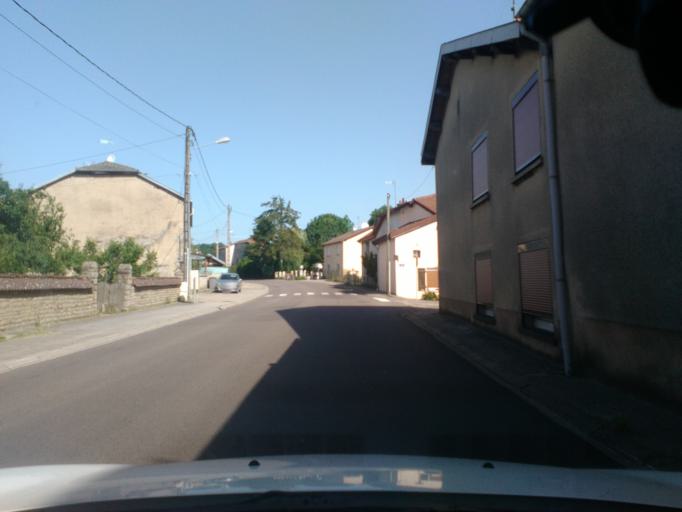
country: FR
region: Lorraine
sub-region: Departement des Vosges
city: Mirecourt
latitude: 48.3094
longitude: 6.1012
